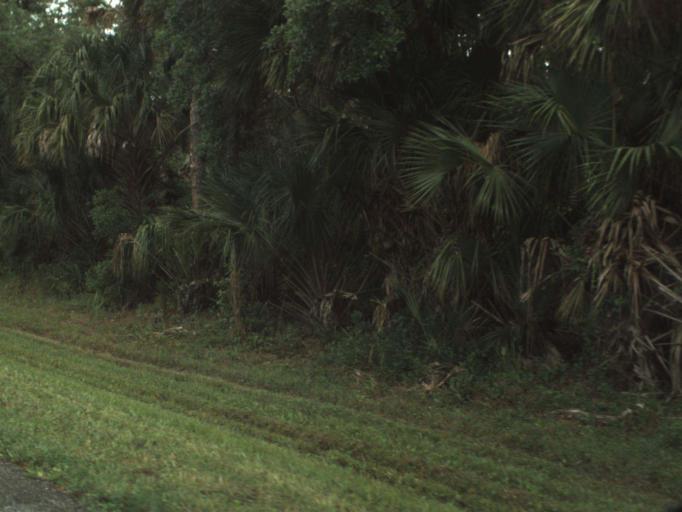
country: US
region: Florida
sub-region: Seminole County
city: Geneva
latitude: 28.6841
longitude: -80.9881
